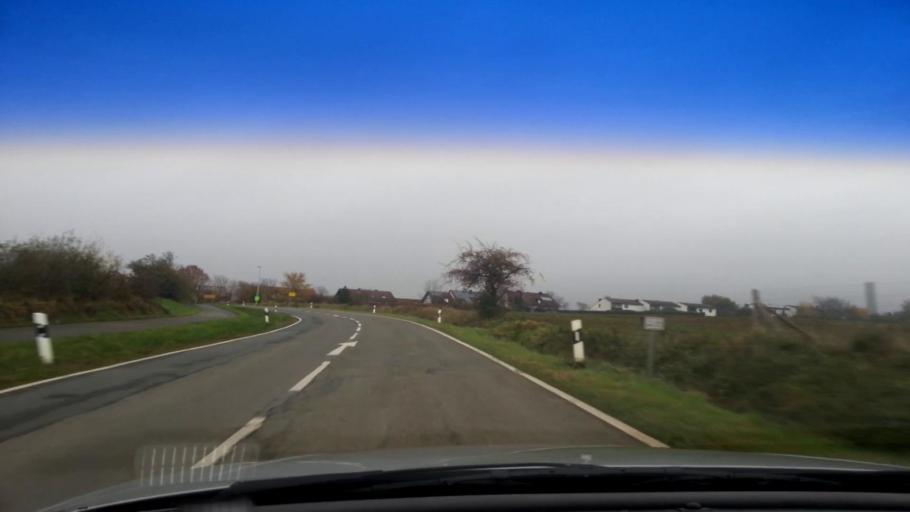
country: DE
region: Bavaria
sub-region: Upper Franconia
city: Litzendorf
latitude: 49.9062
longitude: 11.0125
